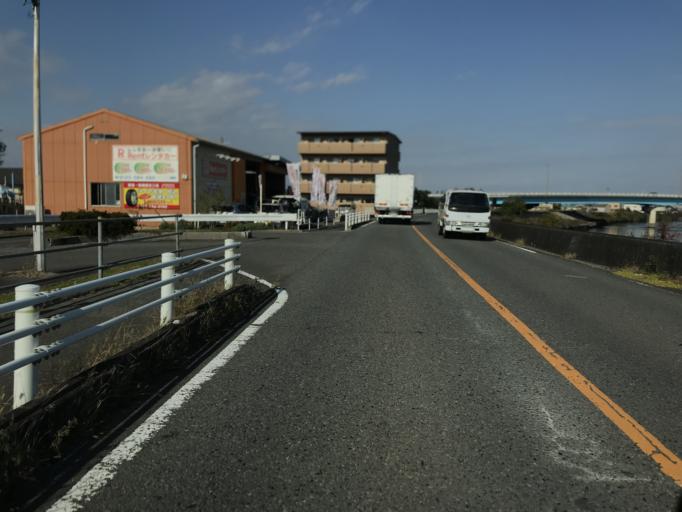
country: JP
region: Aichi
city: Kanie
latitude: 35.1673
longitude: 136.8265
